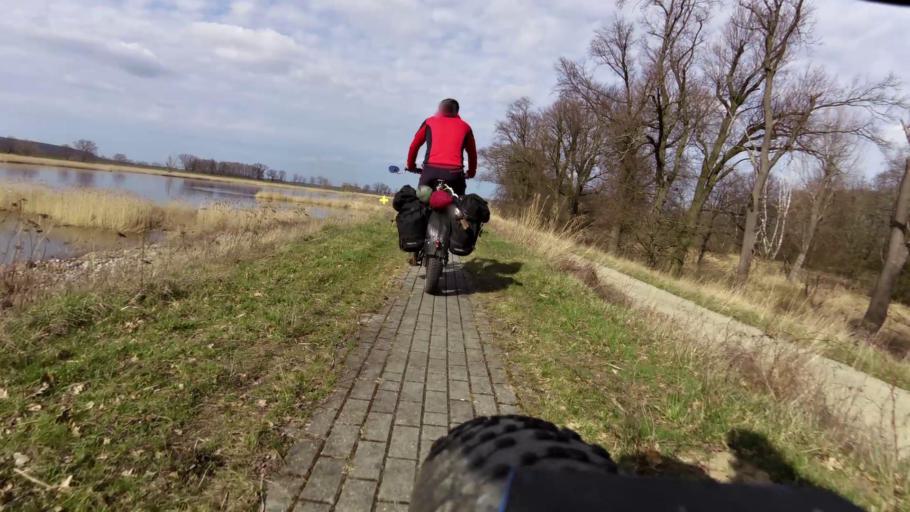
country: DE
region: Brandenburg
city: Reitwein
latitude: 52.4716
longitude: 14.6137
